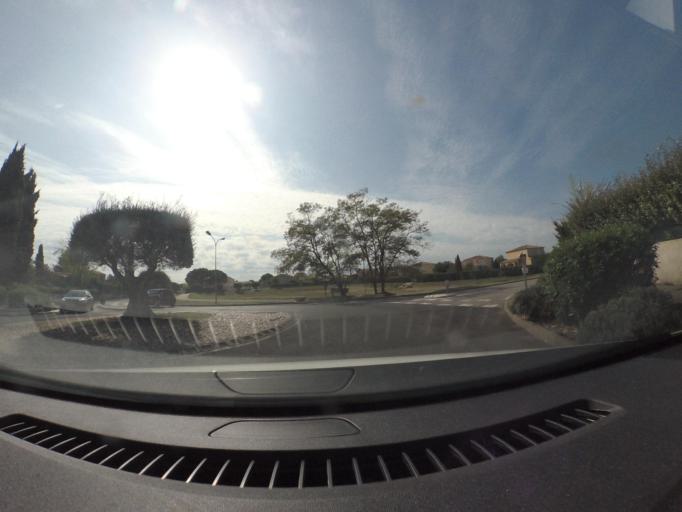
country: FR
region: Languedoc-Roussillon
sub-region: Departement de l'Herault
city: Baillargues
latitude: 43.6576
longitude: 4.0037
